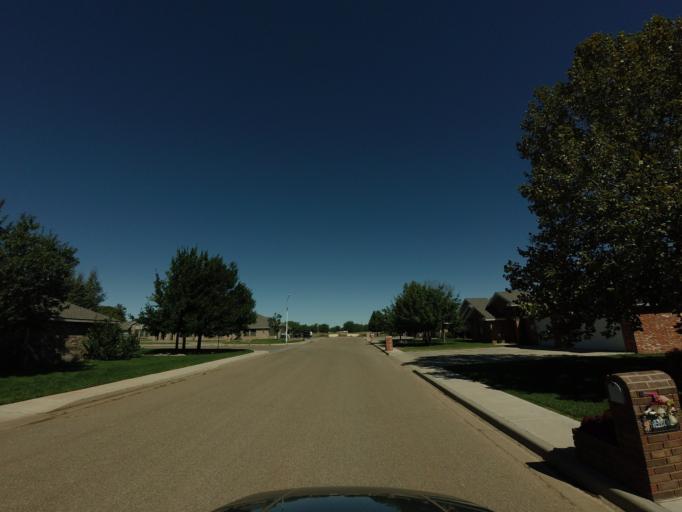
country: US
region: New Mexico
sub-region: Curry County
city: Clovis
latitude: 34.4312
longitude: -103.1721
